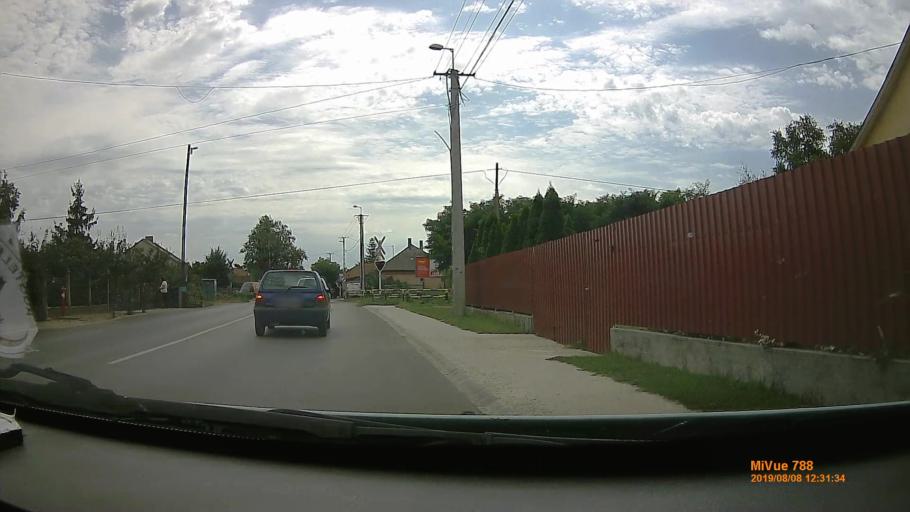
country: HU
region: Szabolcs-Szatmar-Bereg
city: Nyirbator
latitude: 47.8420
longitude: 22.1214
